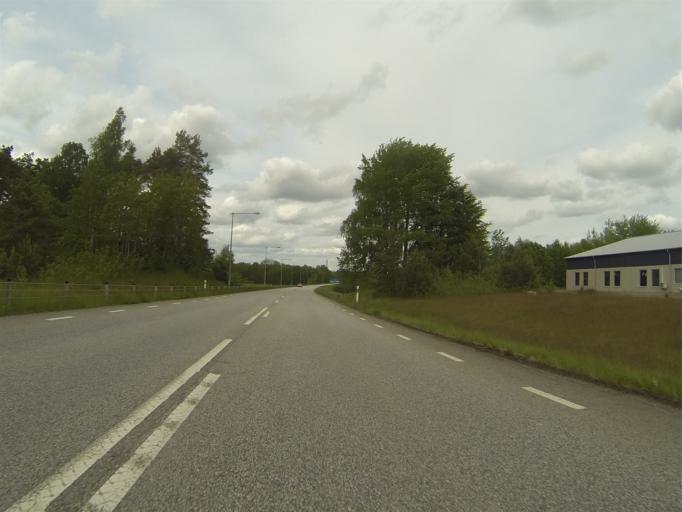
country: SE
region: Skane
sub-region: Sjobo Kommun
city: Sjoebo
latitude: 55.6378
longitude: 13.6827
